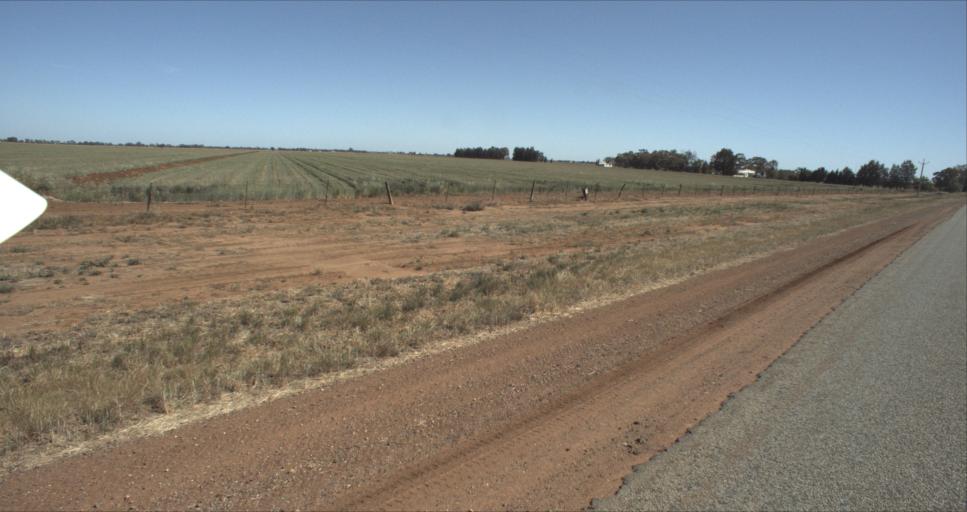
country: AU
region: New South Wales
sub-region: Leeton
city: Leeton
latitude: -34.5479
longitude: 146.3152
